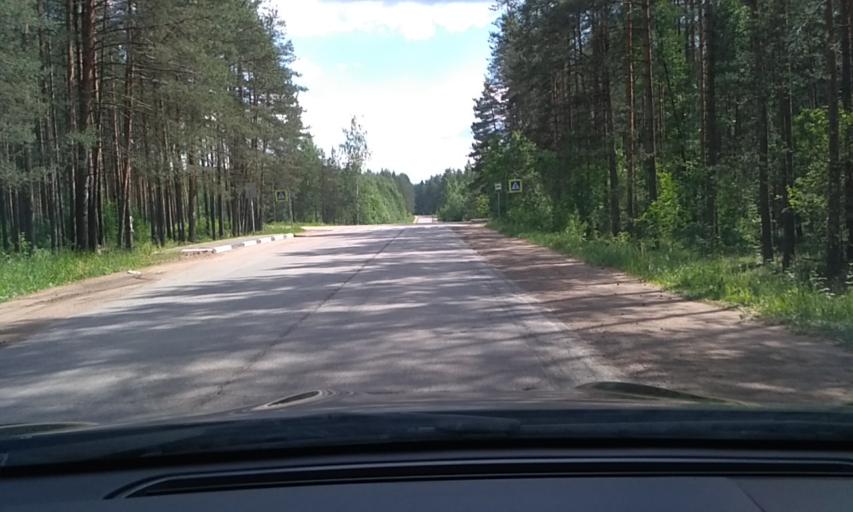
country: RU
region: Leningrad
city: Imeni Sverdlova
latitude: 59.8456
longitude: 30.6866
